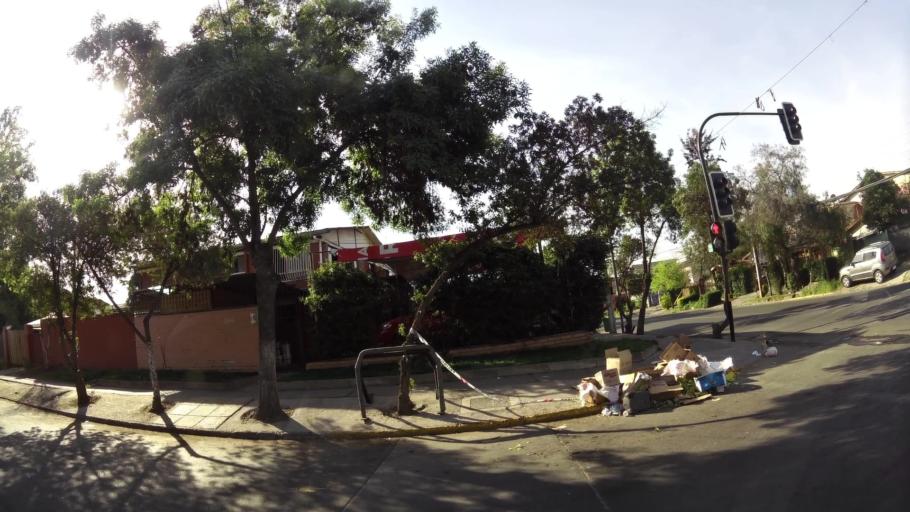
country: CL
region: Santiago Metropolitan
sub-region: Provincia de Santiago
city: Villa Presidente Frei, Nunoa, Santiago, Chile
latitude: -33.5279
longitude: -70.5800
